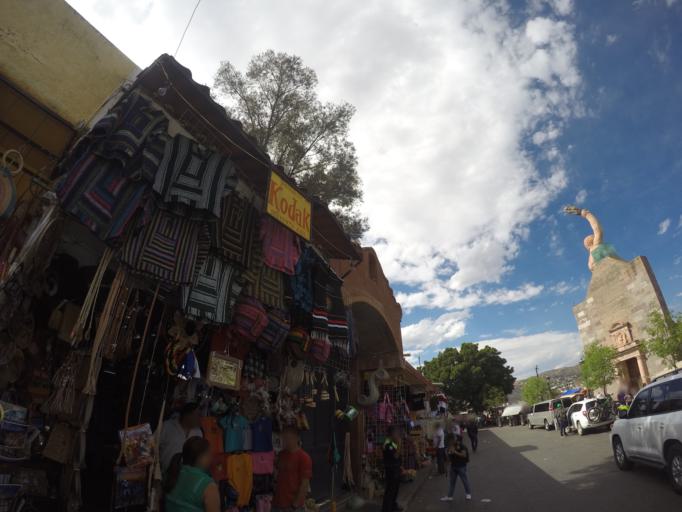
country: MX
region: Guanajuato
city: Guanajuato
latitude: 21.0141
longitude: -101.2544
